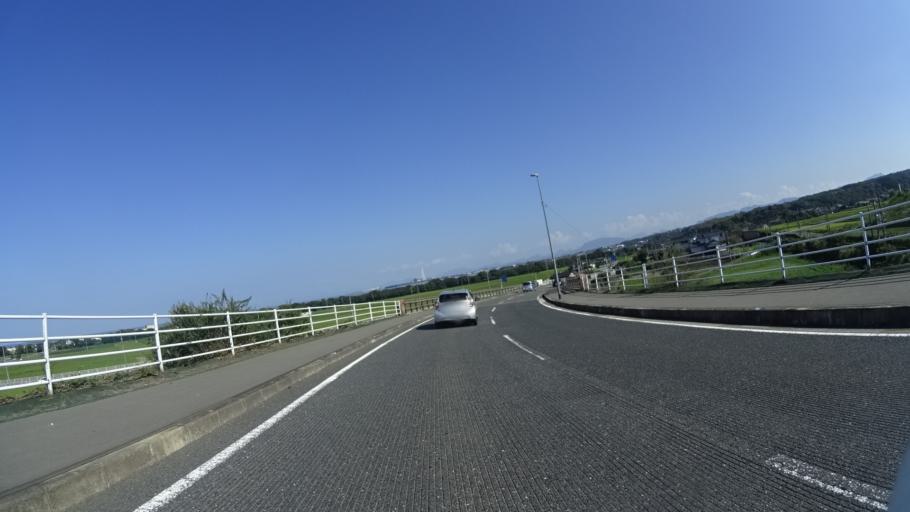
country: JP
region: Fukuoka
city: Shiida
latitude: 33.6459
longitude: 131.0662
